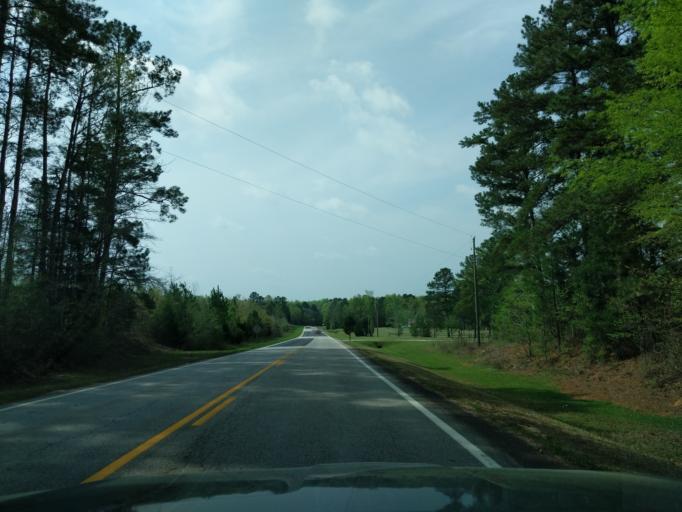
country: US
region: Georgia
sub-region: Lincoln County
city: Lincolnton
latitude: 33.7641
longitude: -82.3769
